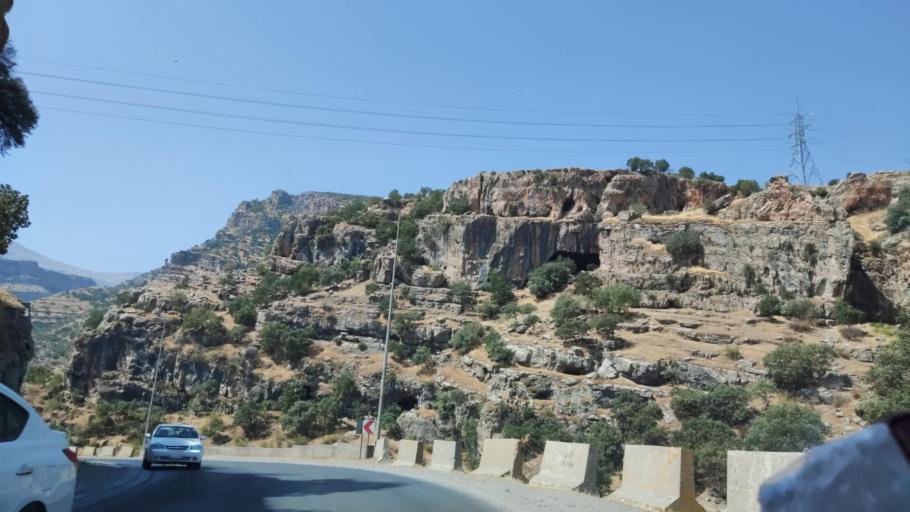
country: IQ
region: Arbil
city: Ruwandiz
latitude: 36.6473
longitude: 44.4970
